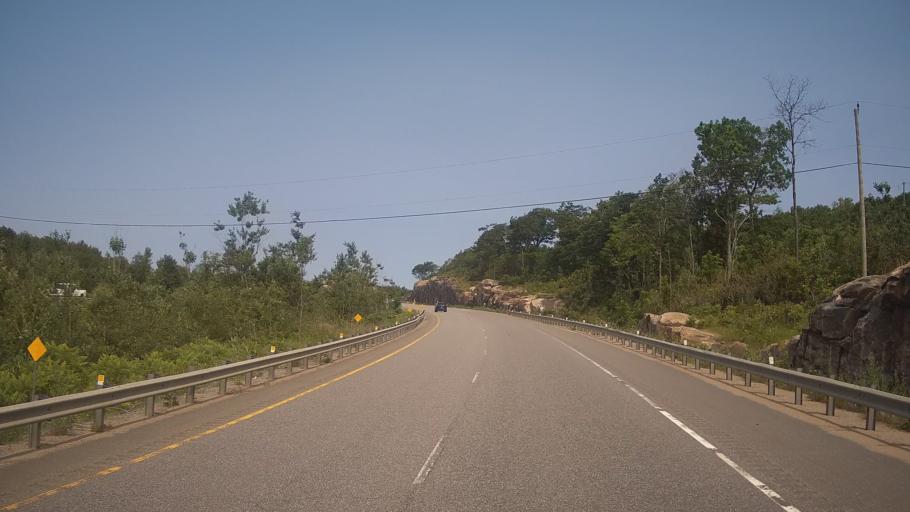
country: CA
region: Ontario
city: Midland
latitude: 44.8811
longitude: -79.7478
